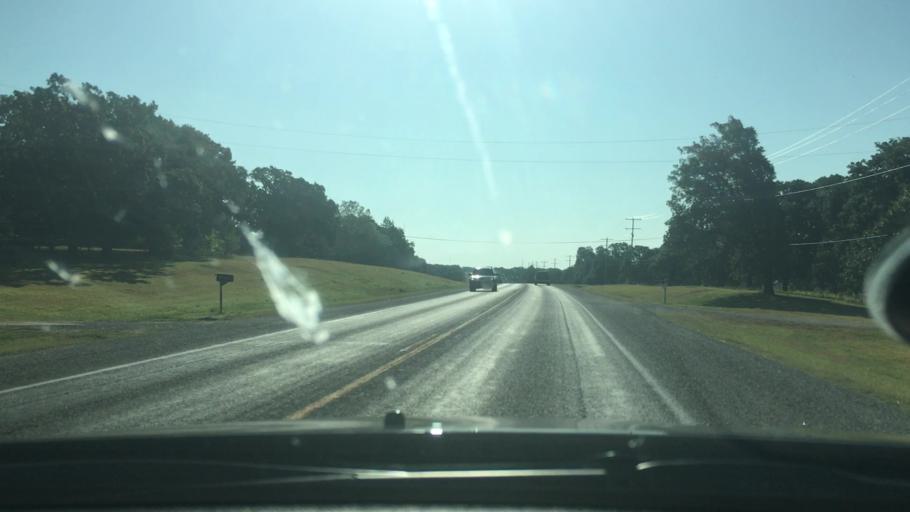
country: US
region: Oklahoma
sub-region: Johnston County
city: Tishomingo
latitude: 34.2369
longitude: -96.7272
